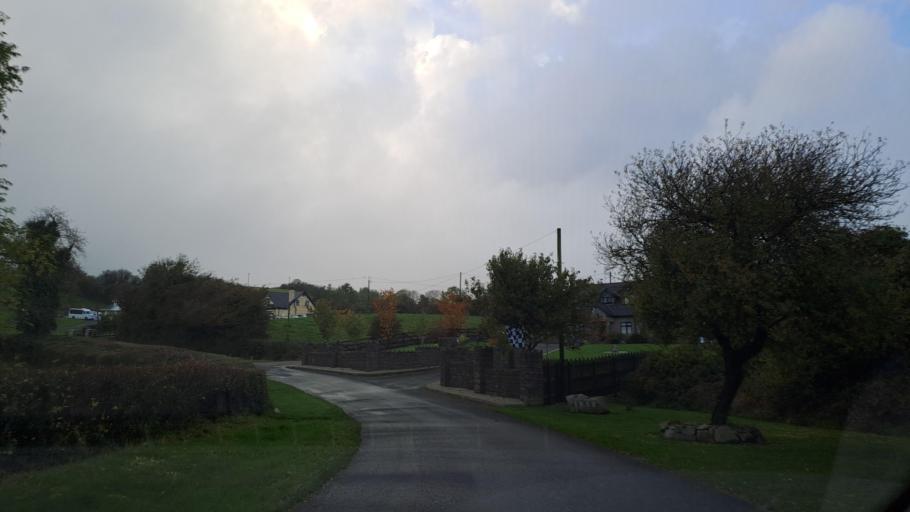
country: IE
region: Ulster
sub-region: An Cabhan
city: Kingscourt
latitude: 53.9700
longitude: -6.7868
